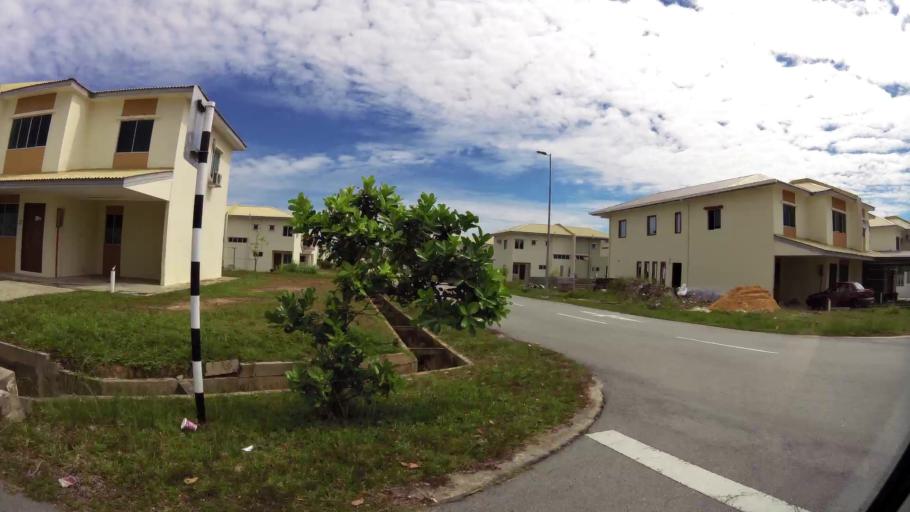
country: BN
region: Brunei and Muara
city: Bandar Seri Begawan
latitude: 4.9826
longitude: 115.0103
